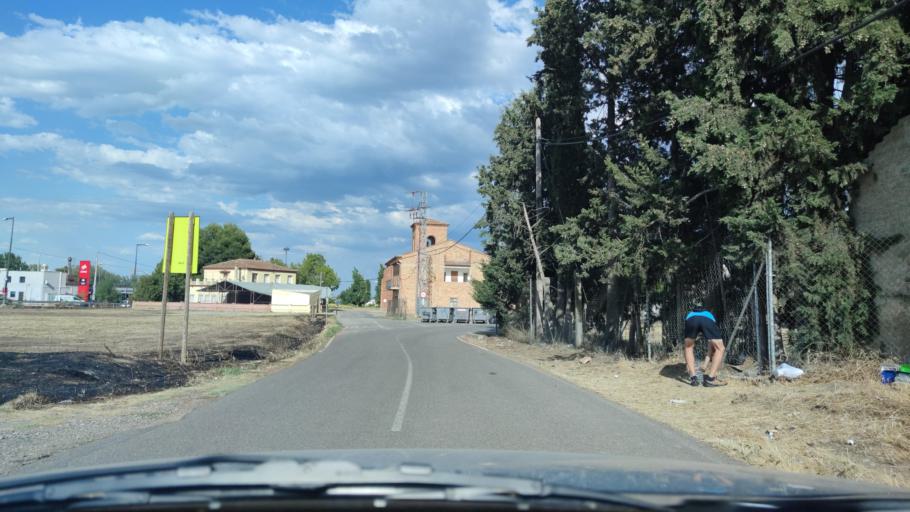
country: ES
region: Catalonia
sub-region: Provincia de Lleida
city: Lleida
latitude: 41.6312
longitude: 0.5914
